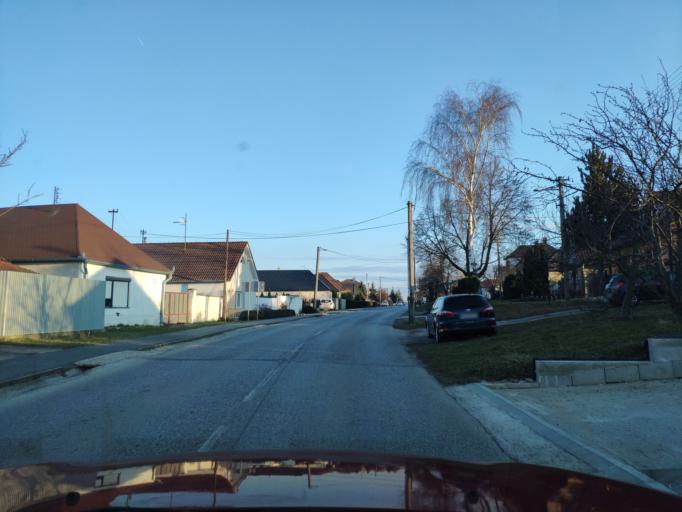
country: SK
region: Nitriansky
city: Sellye
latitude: 48.2738
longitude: 17.8329
